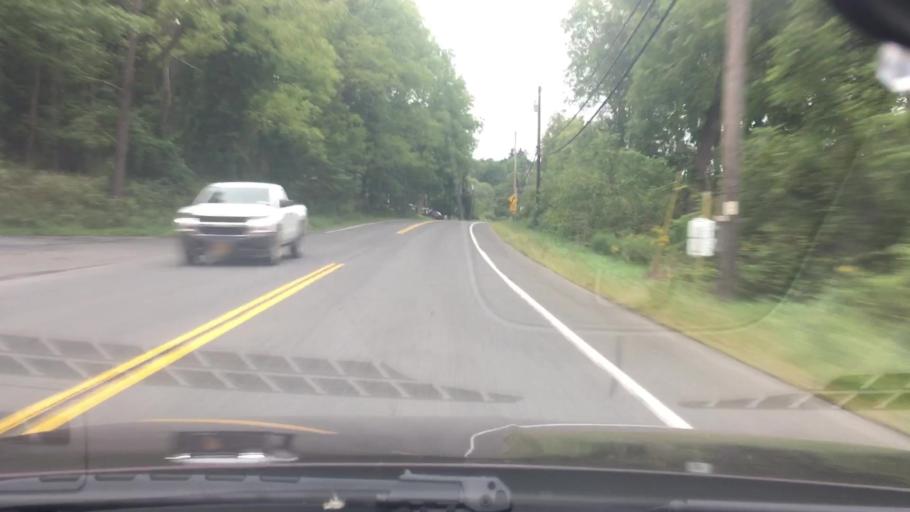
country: US
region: New York
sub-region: Dutchess County
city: Millbrook
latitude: 41.7805
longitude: -73.7498
